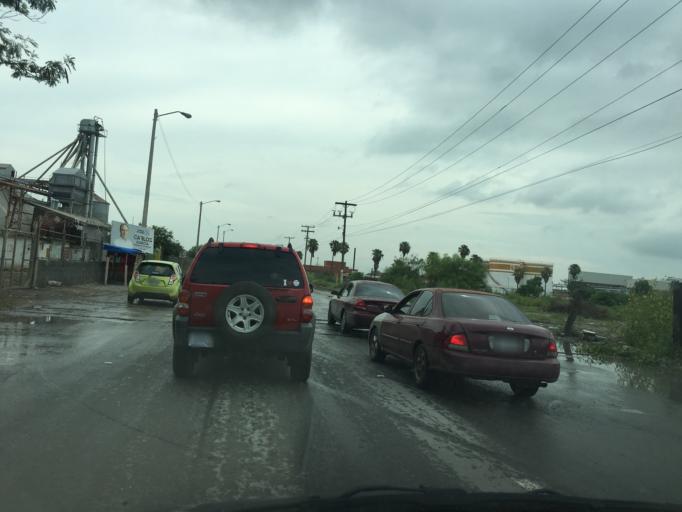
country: MX
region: Tamaulipas
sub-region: Matamoros
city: Heroica Matamoros
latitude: 25.8775
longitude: -97.5283
